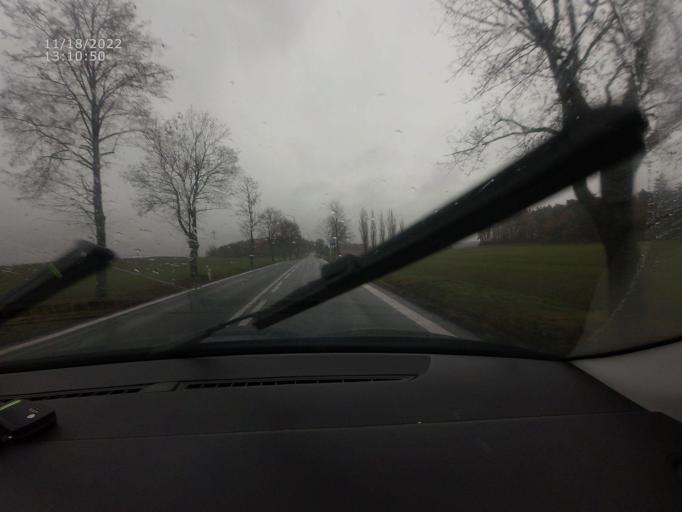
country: CZ
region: Plzensky
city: Hradek
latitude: 49.3300
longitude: 13.5705
